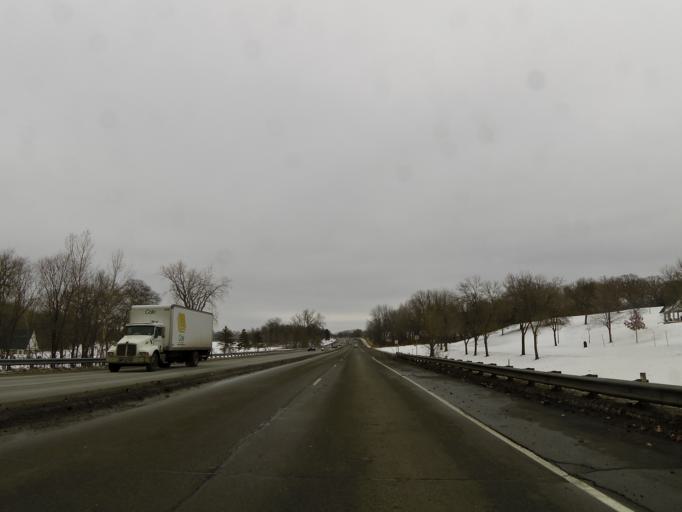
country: US
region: Minnesota
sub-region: Ramsey County
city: Little Canada
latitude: 45.0006
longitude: -93.0639
